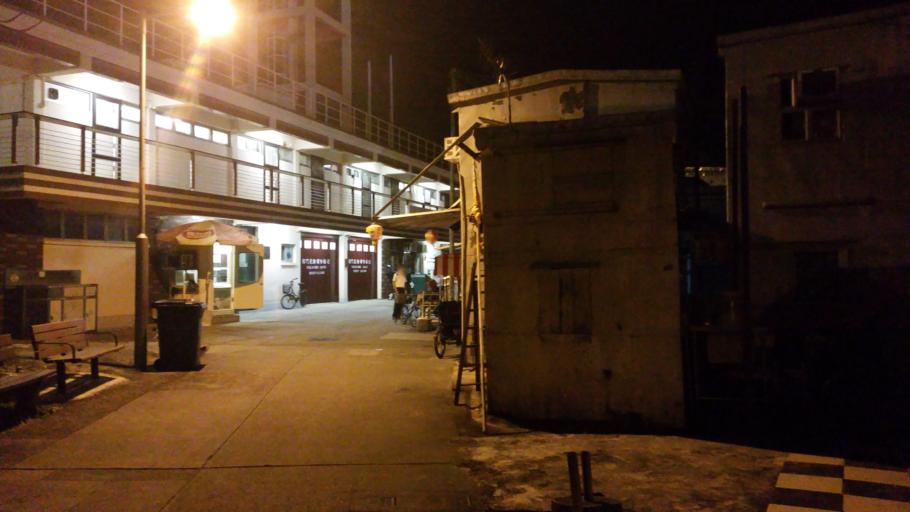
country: HK
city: Tai O
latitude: 22.2552
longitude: 113.8601
